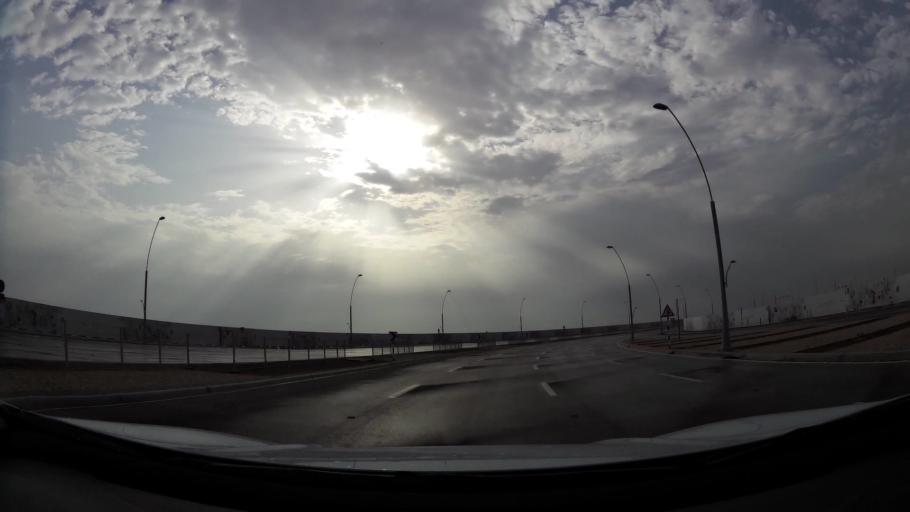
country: AE
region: Abu Dhabi
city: Abu Dhabi
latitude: 24.5069
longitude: 54.4135
